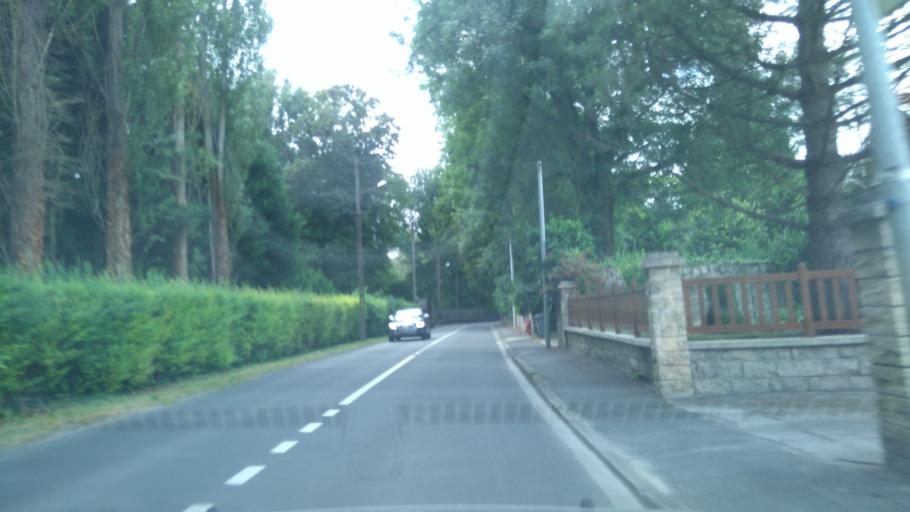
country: FR
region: Picardie
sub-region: Departement de l'Oise
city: Gouvieux
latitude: 49.1993
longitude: 2.4231
